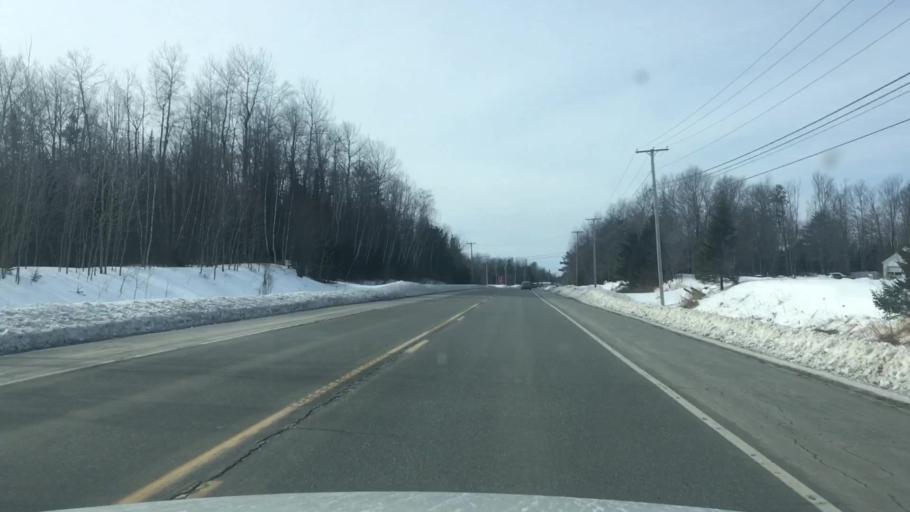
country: US
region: Maine
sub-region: Penobscot County
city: Kenduskeag
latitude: 44.9118
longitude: -68.9027
